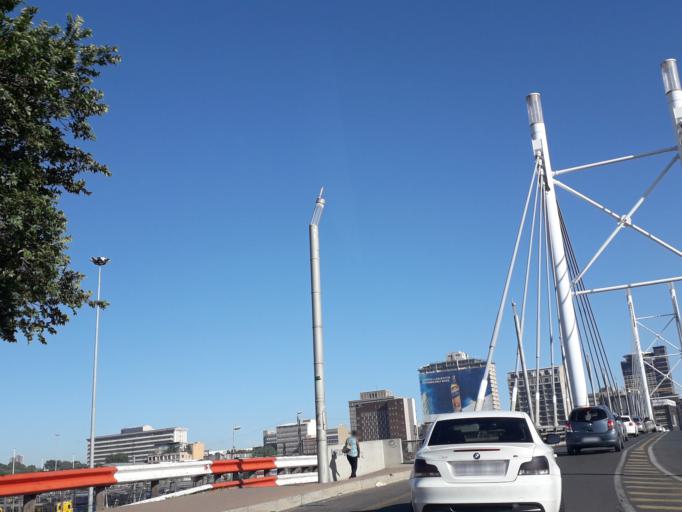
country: ZA
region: Gauteng
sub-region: City of Johannesburg Metropolitan Municipality
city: Johannesburg
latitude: -26.1982
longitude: 28.0346
